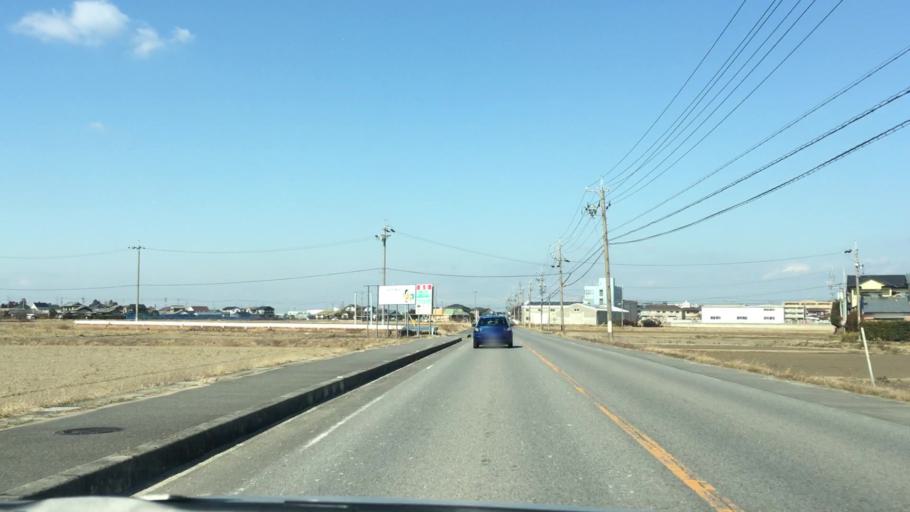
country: JP
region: Aichi
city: Anjo
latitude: 34.9837
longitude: 137.1179
